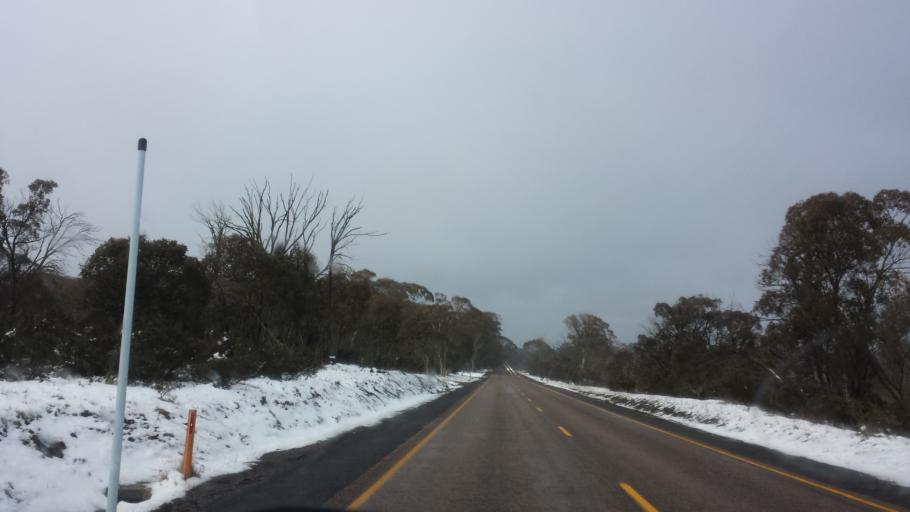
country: AU
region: Victoria
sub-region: Alpine
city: Mount Beauty
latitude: -37.0325
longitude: 147.2991
